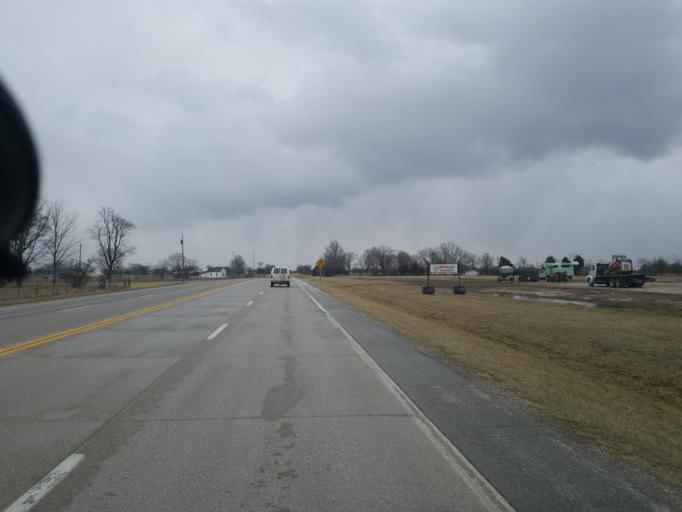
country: US
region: Missouri
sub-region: Macon County
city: Macon
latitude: 39.7771
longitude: -92.4772
